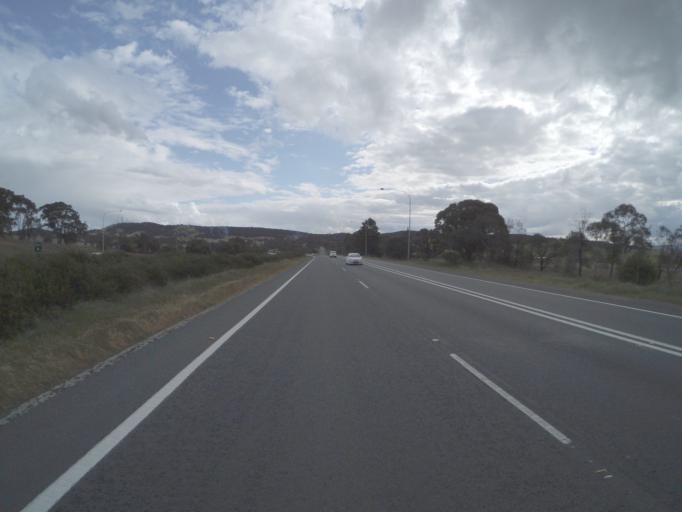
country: AU
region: New South Wales
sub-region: Goulburn Mulwaree
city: Goulburn
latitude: -34.7388
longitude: 149.7788
